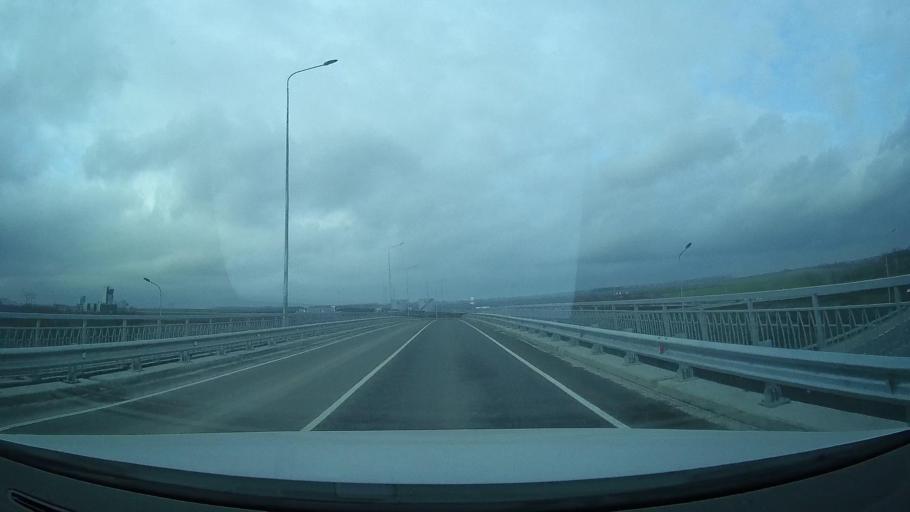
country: RU
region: Rostov
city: Grushevskaya
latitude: 47.4933
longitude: 39.9514
